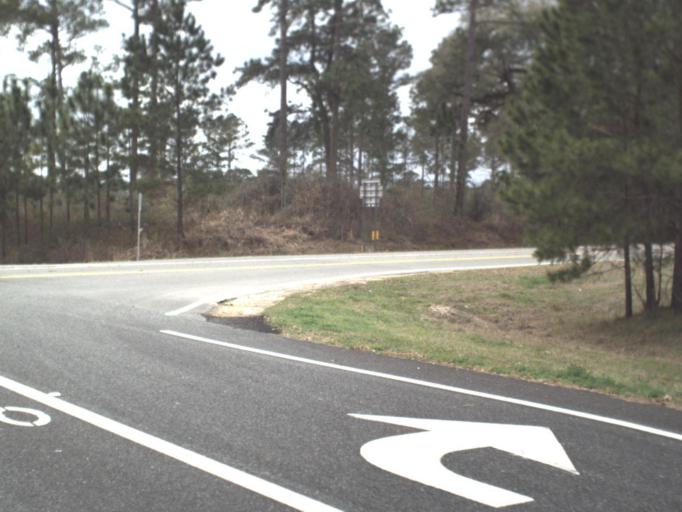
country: US
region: Georgia
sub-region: Grady County
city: Cairo
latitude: 30.6675
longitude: -84.1644
